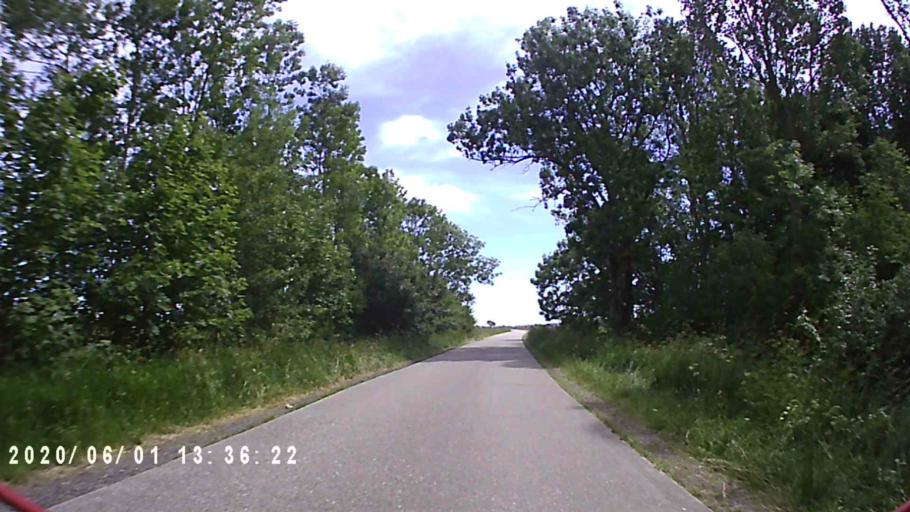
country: NL
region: Friesland
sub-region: Gemeente Littenseradiel
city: Wommels
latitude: 53.0869
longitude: 5.5870
